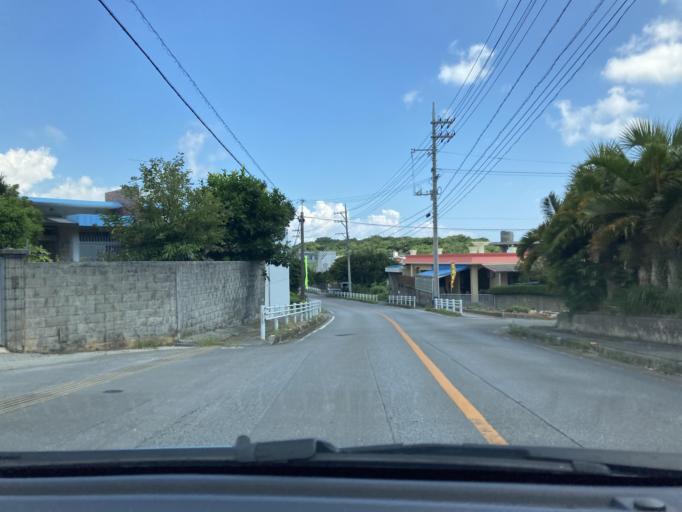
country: JP
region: Okinawa
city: Tomigusuku
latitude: 26.1493
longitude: 127.7911
